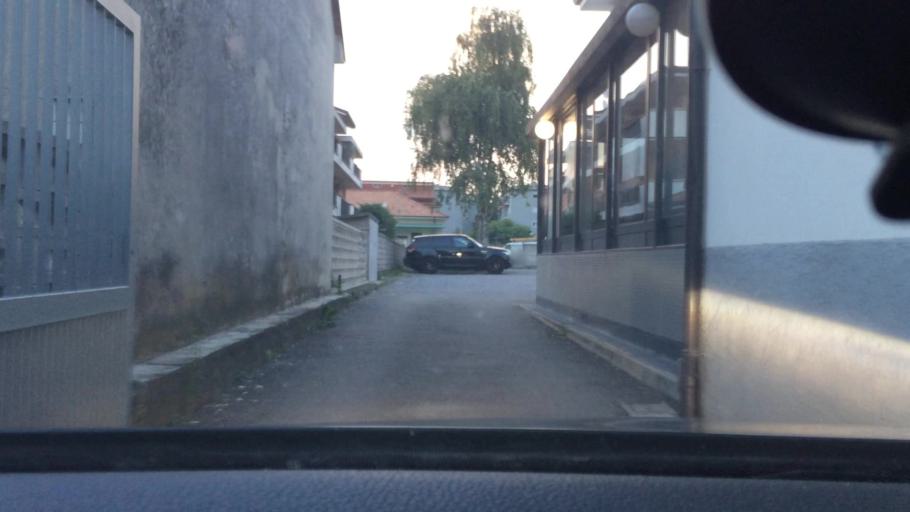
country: IT
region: Lombardy
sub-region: Provincia di Varese
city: Cislago
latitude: 45.6502
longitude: 8.9869
